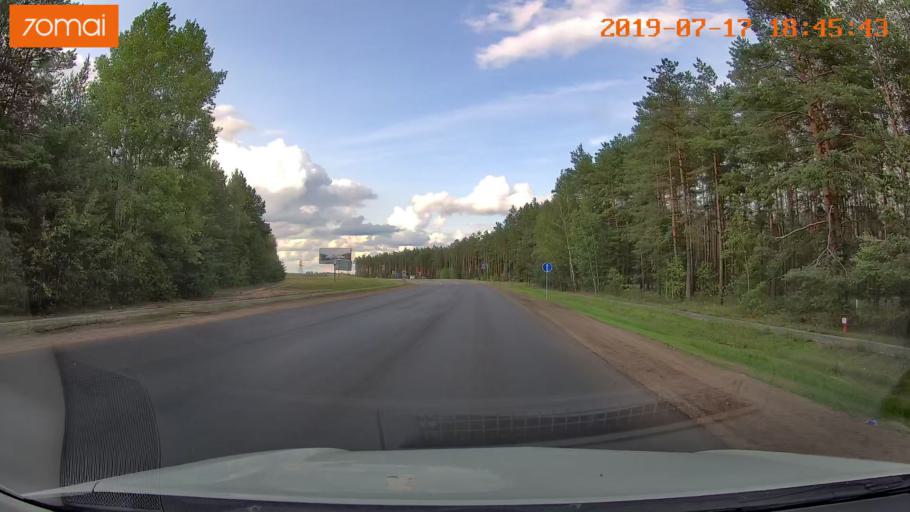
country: BY
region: Mogilev
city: Asipovichy
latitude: 53.3272
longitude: 28.6581
